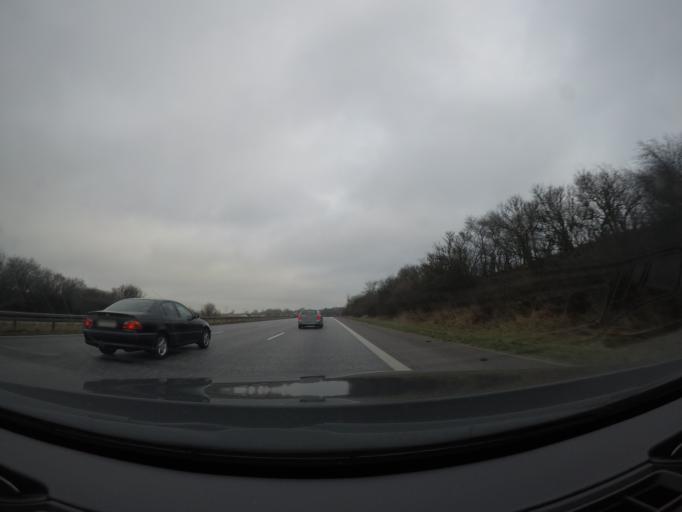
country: DK
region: South Denmark
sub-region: Fredericia Kommune
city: Taulov
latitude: 55.5474
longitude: 9.5385
